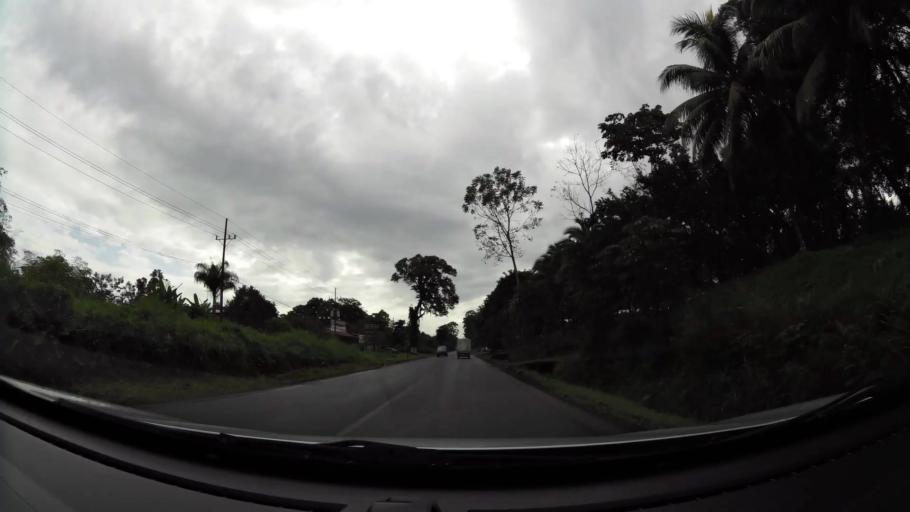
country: CR
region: Limon
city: Pocora
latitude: 10.1450
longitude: -83.5756
